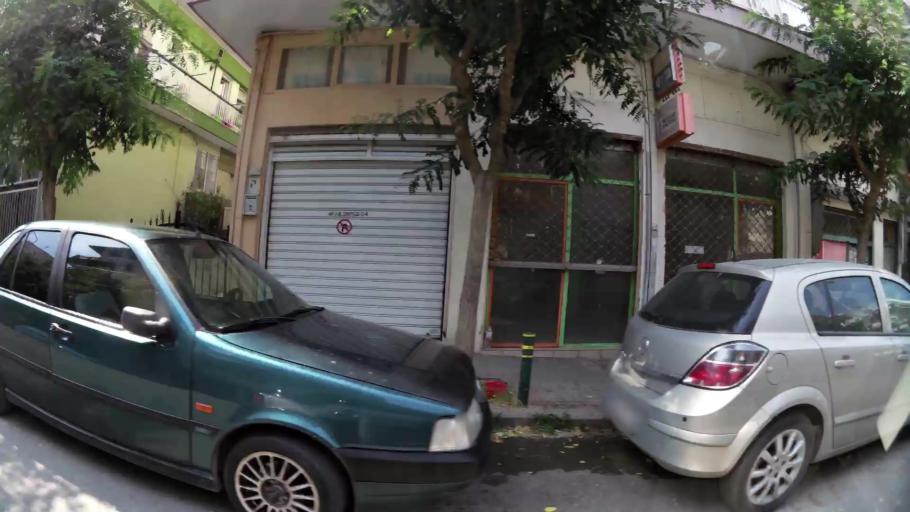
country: GR
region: Central Macedonia
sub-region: Nomos Thessalonikis
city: Sykies
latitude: 40.6472
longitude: 22.9421
